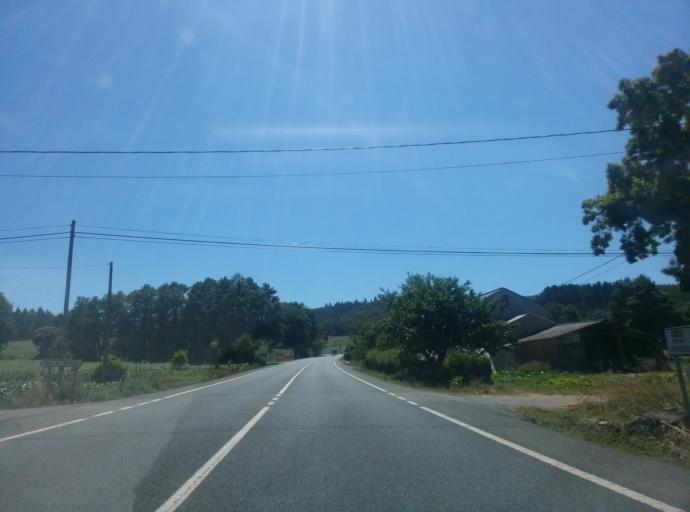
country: ES
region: Galicia
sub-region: Provincia de Lugo
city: Meira
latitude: 43.2168
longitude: -7.3209
